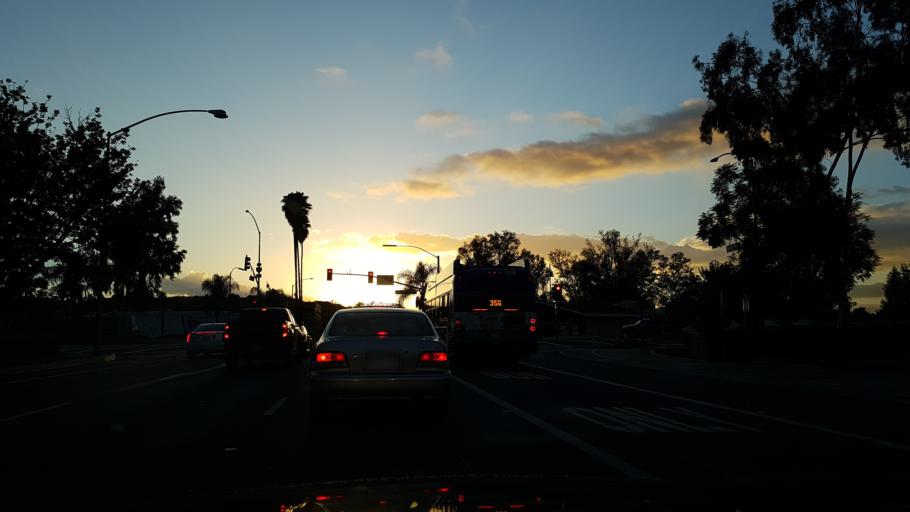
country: US
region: California
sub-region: San Diego County
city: Escondido
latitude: 33.1203
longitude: -117.0867
